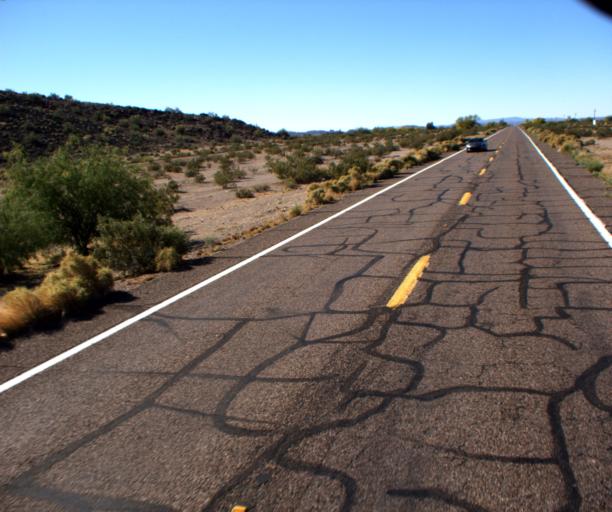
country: US
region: Arizona
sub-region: Maricopa County
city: Gila Bend
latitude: 32.7549
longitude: -112.8245
